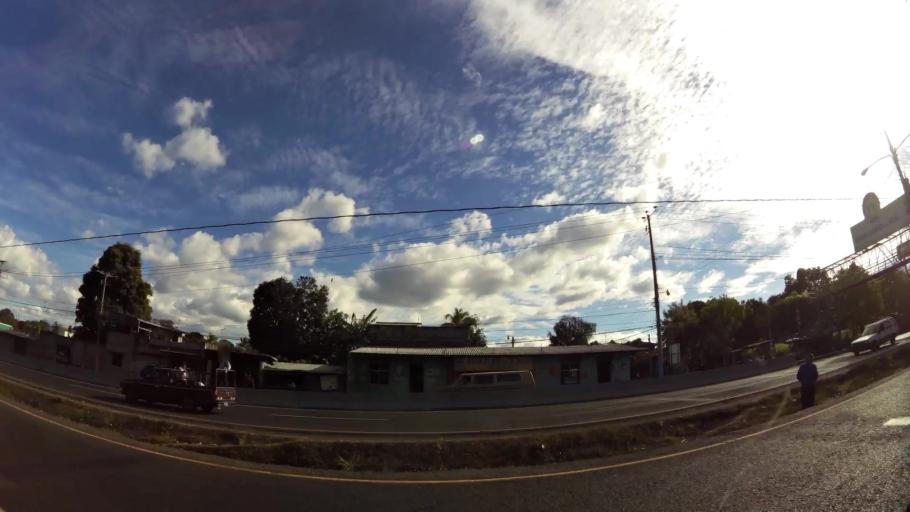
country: SV
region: San Salvador
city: Ilopango
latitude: 13.7343
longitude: -89.0618
